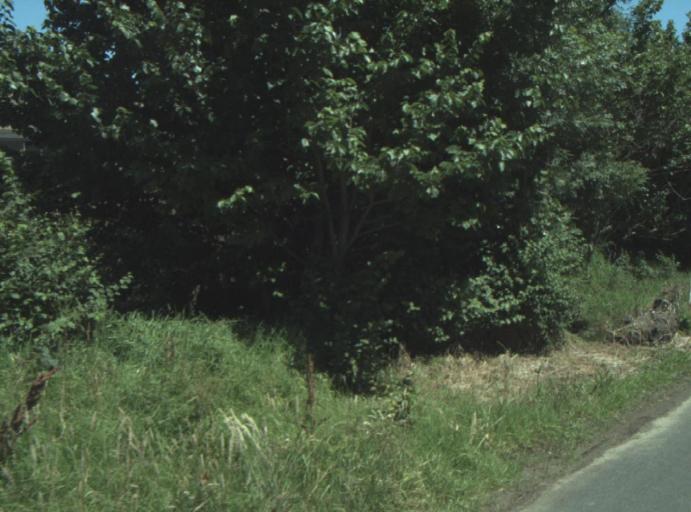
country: AU
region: Victoria
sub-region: Greater Geelong
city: Breakwater
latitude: -38.1942
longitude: 144.3599
